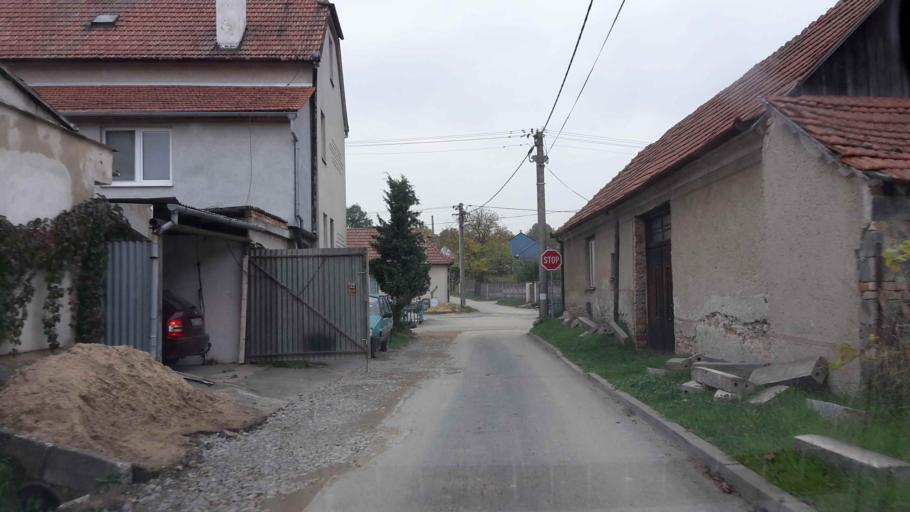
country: CZ
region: South Moravian
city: Damborice
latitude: 49.0398
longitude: 16.9679
